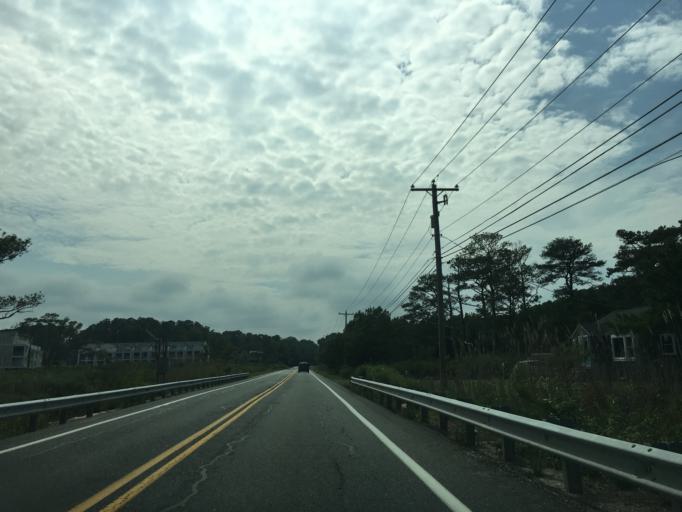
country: US
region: Delaware
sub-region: Sussex County
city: Bethany Beach
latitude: 38.5557
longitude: -75.0633
